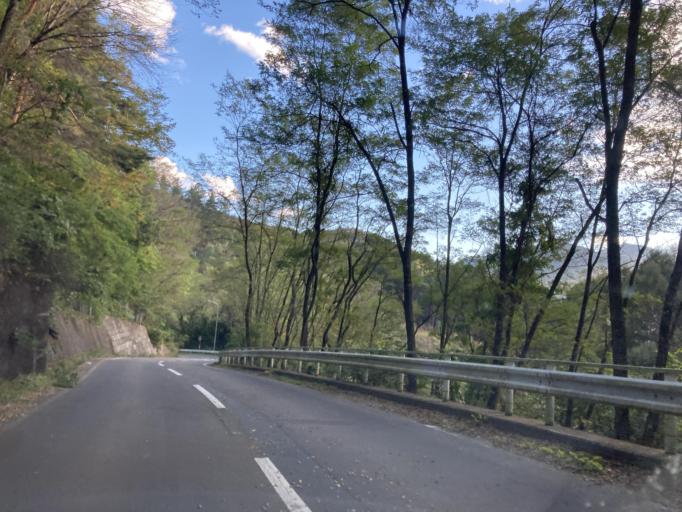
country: JP
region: Nagano
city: Ueda
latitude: 36.4009
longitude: 138.1021
